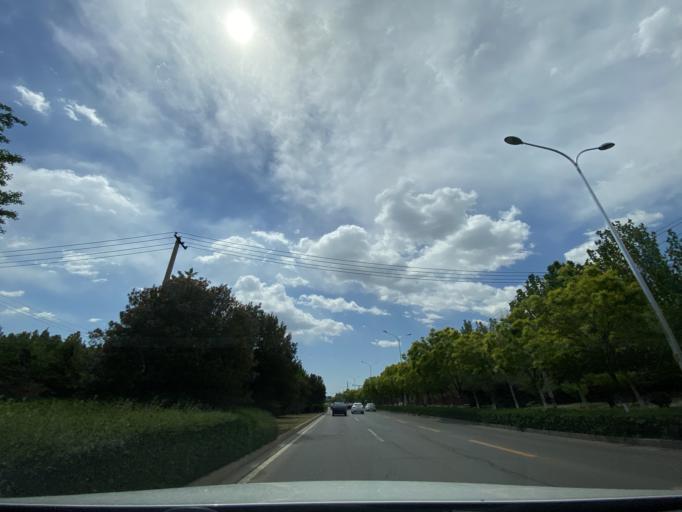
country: CN
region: Beijing
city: Sijiqing
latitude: 39.9436
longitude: 116.2408
